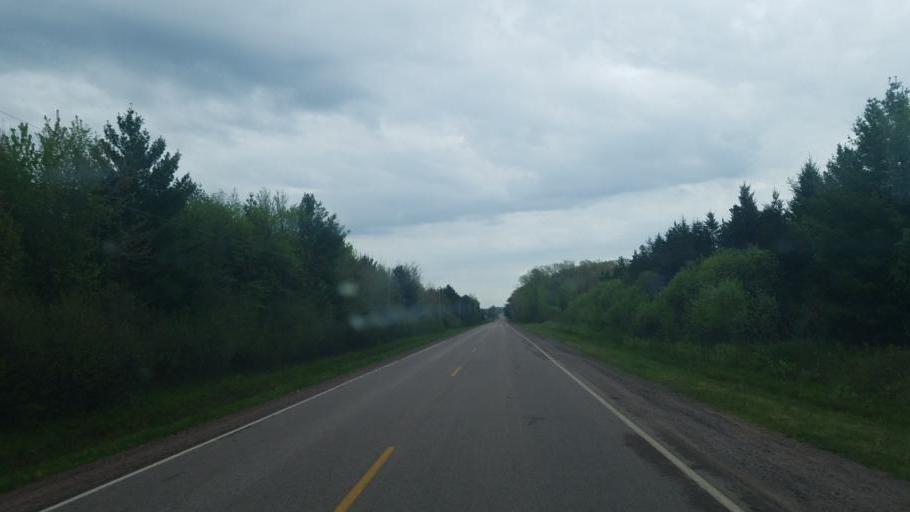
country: US
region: Wisconsin
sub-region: Wood County
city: Marshfield
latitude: 44.5609
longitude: -90.2999
